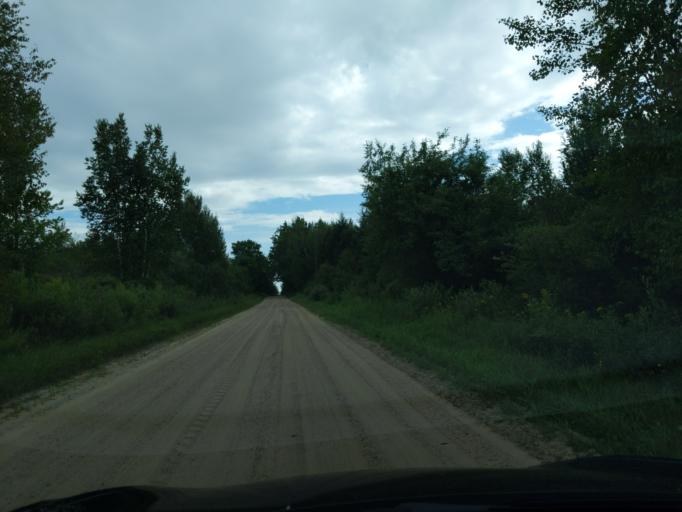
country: US
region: Michigan
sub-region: Clare County
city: Harrison
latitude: 43.9937
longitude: -85.0083
